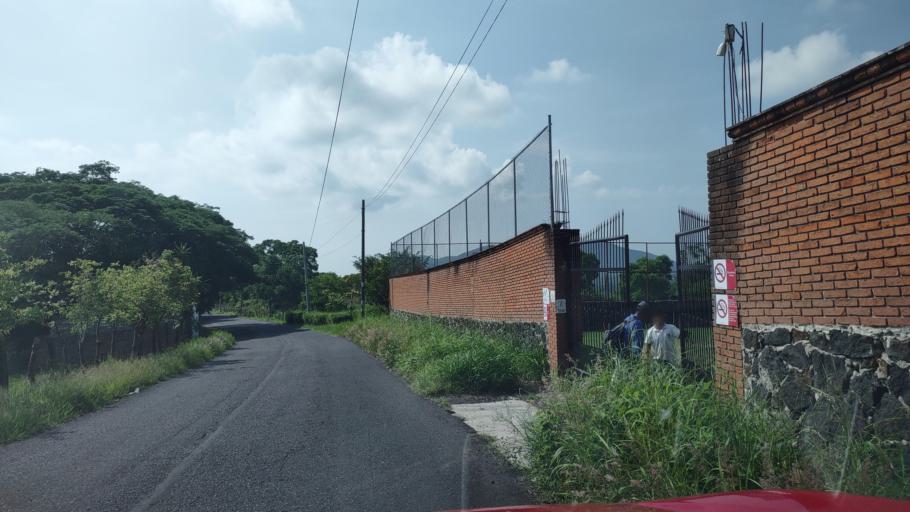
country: MX
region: Veracruz
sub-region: Coatepec
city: Bella Esperanza
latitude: 19.4527
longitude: -96.8306
